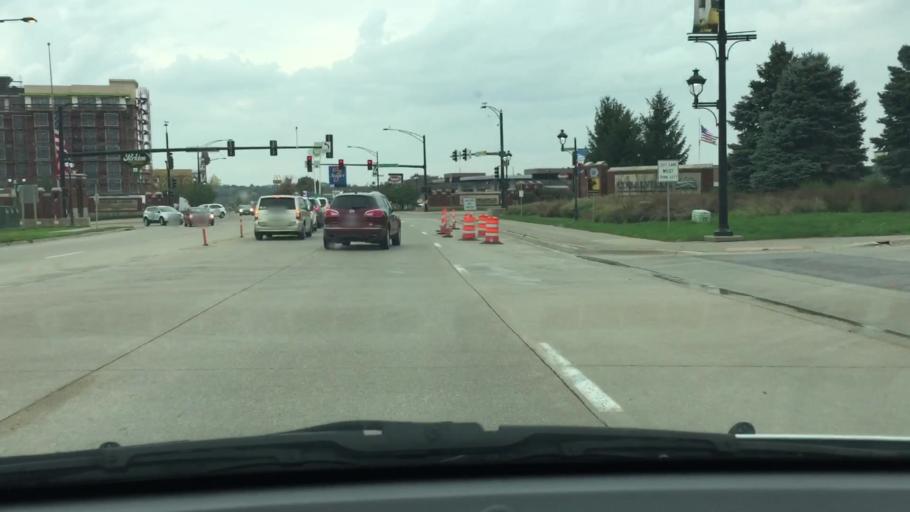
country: US
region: Iowa
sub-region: Johnson County
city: Coralville
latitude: 41.6826
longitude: -91.5656
